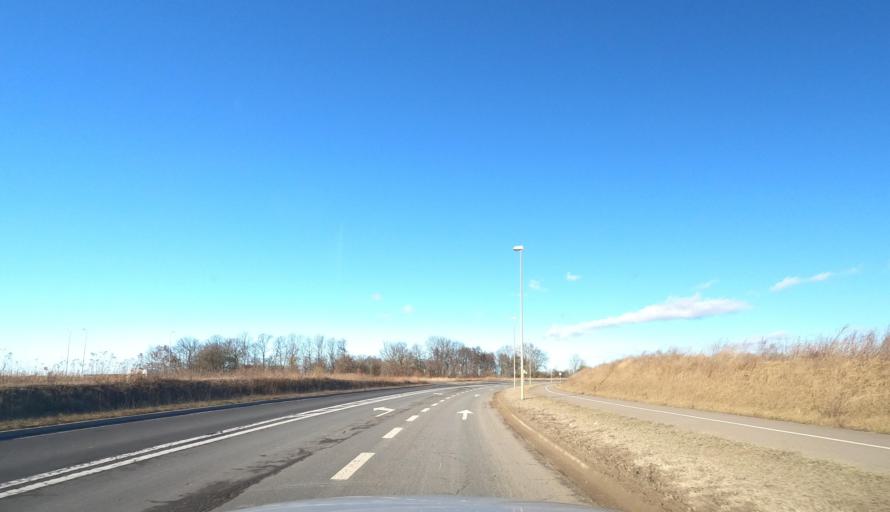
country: PL
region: West Pomeranian Voivodeship
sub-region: Powiat pyrzycki
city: Warnice
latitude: 53.2934
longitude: 14.9588
